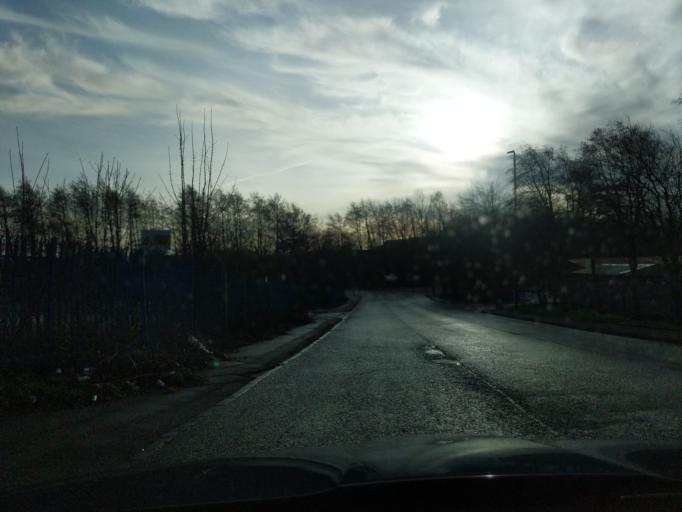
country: GB
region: England
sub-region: Borough of North Tyneside
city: Wallsend
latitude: 54.9842
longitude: -1.5380
